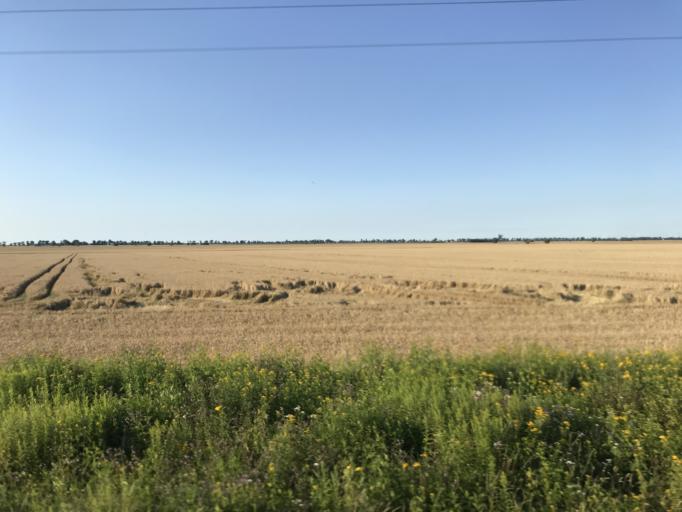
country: PL
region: Pomeranian Voivodeship
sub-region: Powiat malborski
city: Lisewo Malborskie
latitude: 54.0887
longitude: 18.8517
